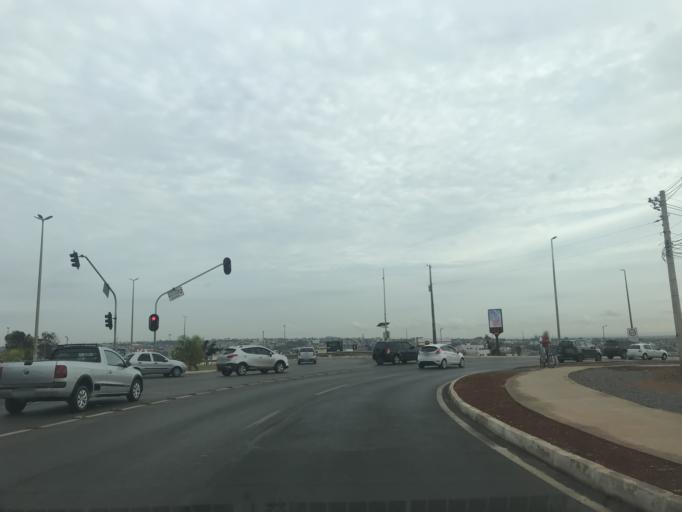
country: BR
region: Federal District
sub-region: Brasilia
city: Brasilia
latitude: -15.8353
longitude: -48.0524
